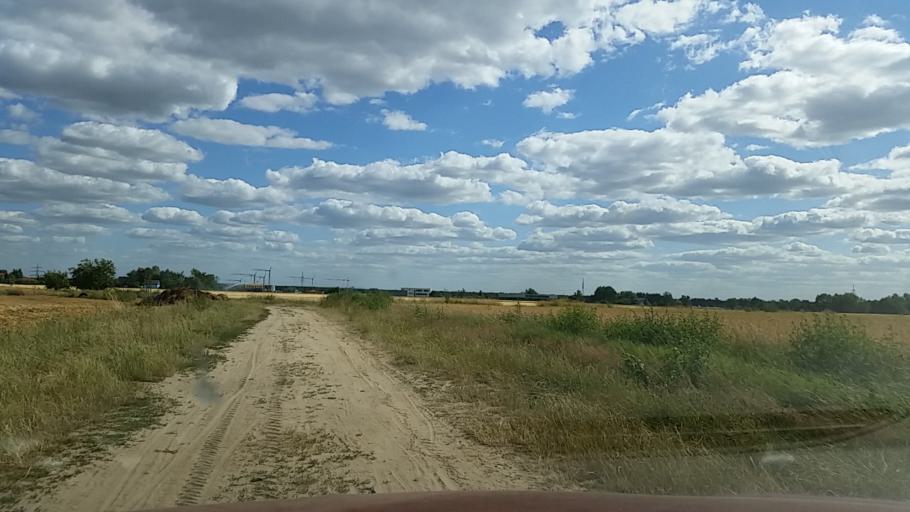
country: DE
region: Lower Saxony
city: Tappenbeck
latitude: 52.4720
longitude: 10.7281
